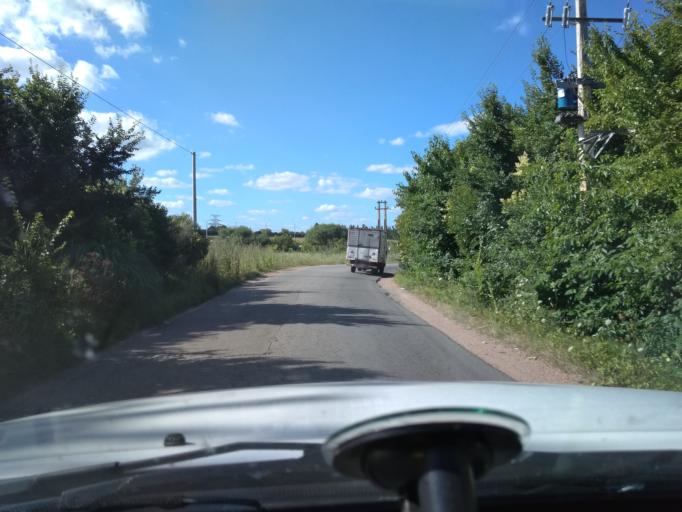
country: UY
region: Canelones
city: La Paz
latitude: -34.7928
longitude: -56.2117
